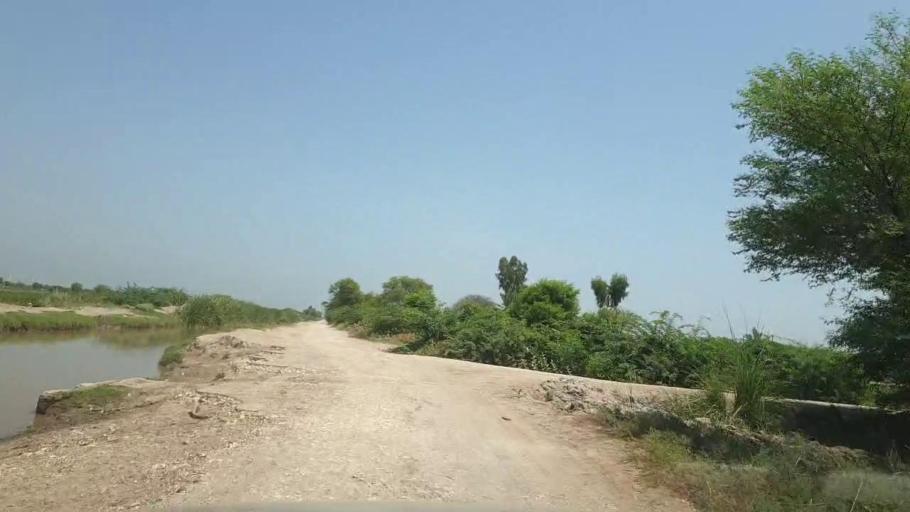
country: PK
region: Sindh
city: Rohri
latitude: 27.6344
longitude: 69.1006
